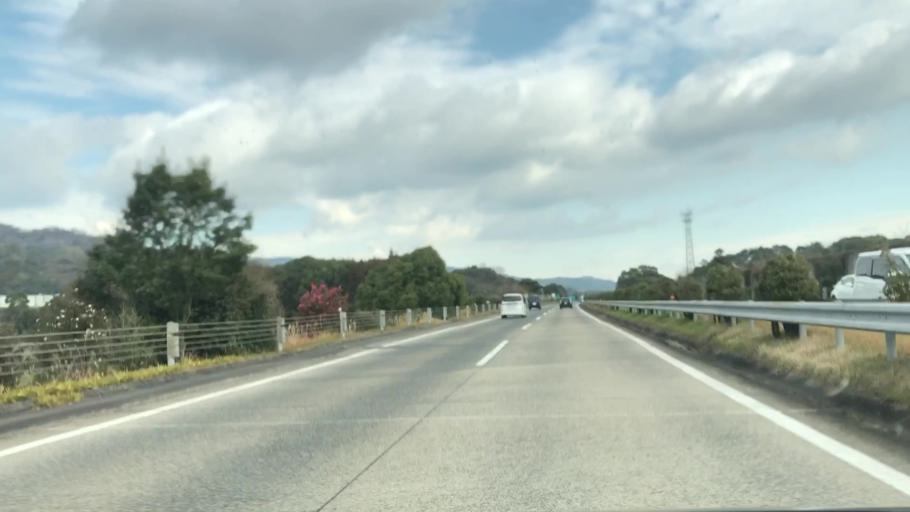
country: JP
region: Saga Prefecture
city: Kanzakimachi-kanzaki
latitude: 33.3504
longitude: 130.3771
